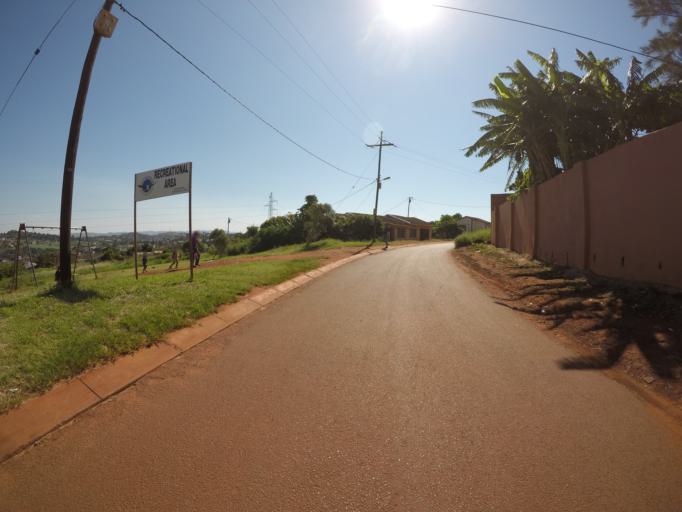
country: ZA
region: KwaZulu-Natal
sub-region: uThungulu District Municipality
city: Empangeni
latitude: -28.7741
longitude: 31.8798
